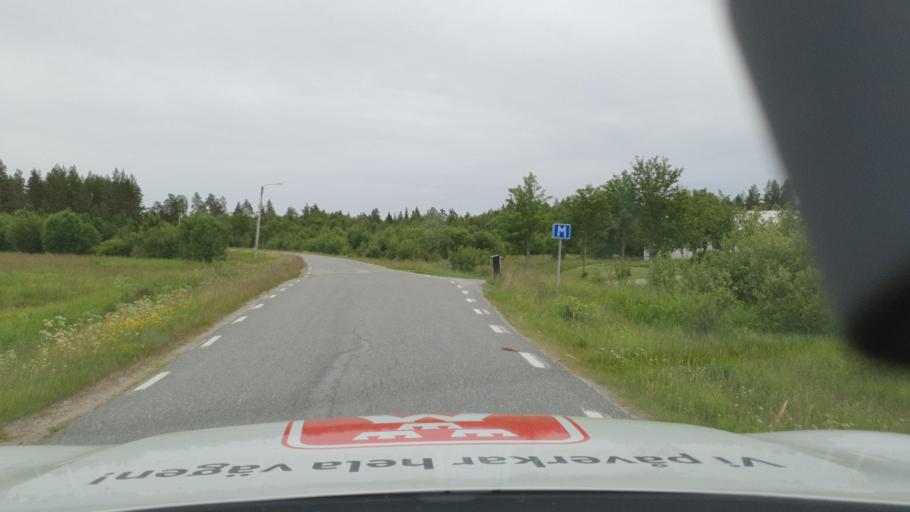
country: SE
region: Vaesterbotten
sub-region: Nordmalings Kommun
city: Nordmaling
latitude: 63.5001
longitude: 19.4192
